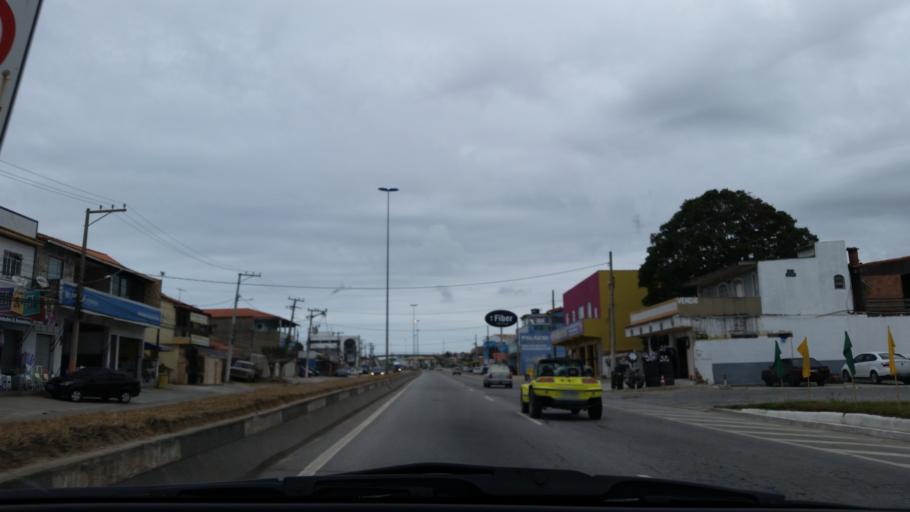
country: BR
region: Rio de Janeiro
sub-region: Sao Pedro Da Aldeia
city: Sao Pedro da Aldeia
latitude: -22.8308
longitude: -42.1298
